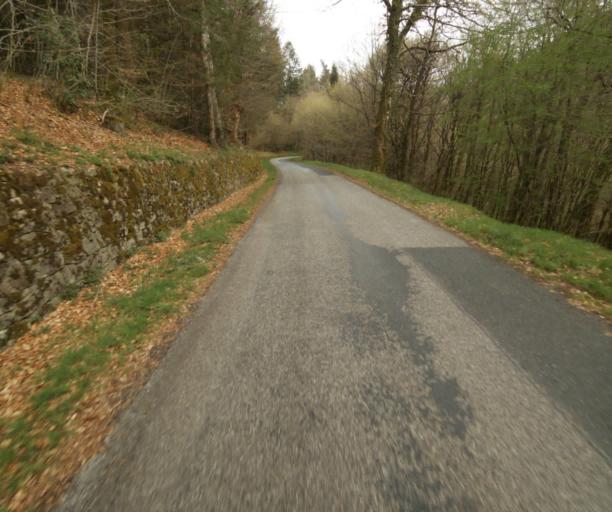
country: FR
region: Limousin
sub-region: Departement de la Correze
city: Argentat
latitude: 45.1934
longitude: 1.9632
